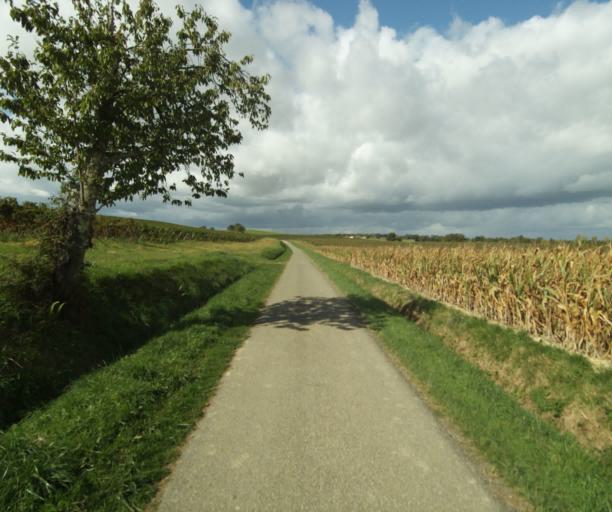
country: FR
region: Midi-Pyrenees
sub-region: Departement du Gers
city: Nogaro
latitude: 43.8466
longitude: -0.0295
